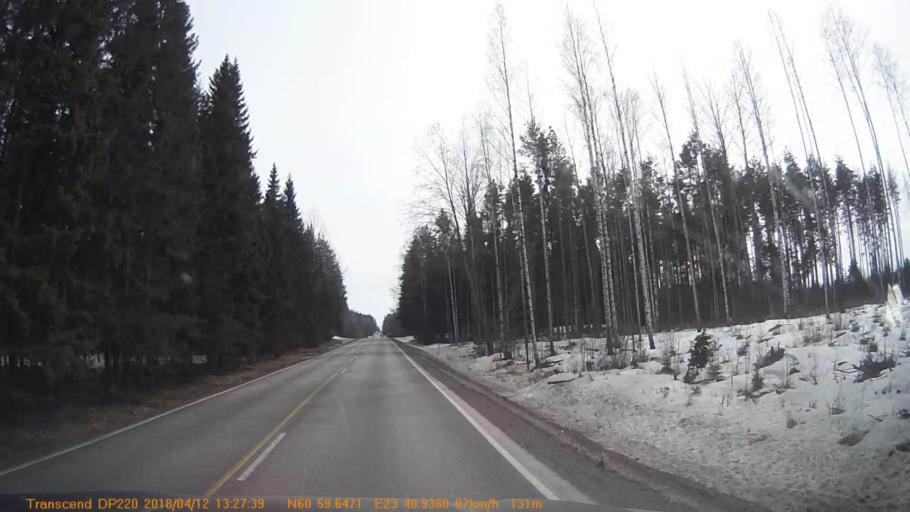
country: FI
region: Pirkanmaa
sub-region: Etelae-Pirkanmaa
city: Kylmaekoski
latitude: 60.9939
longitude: 23.6824
